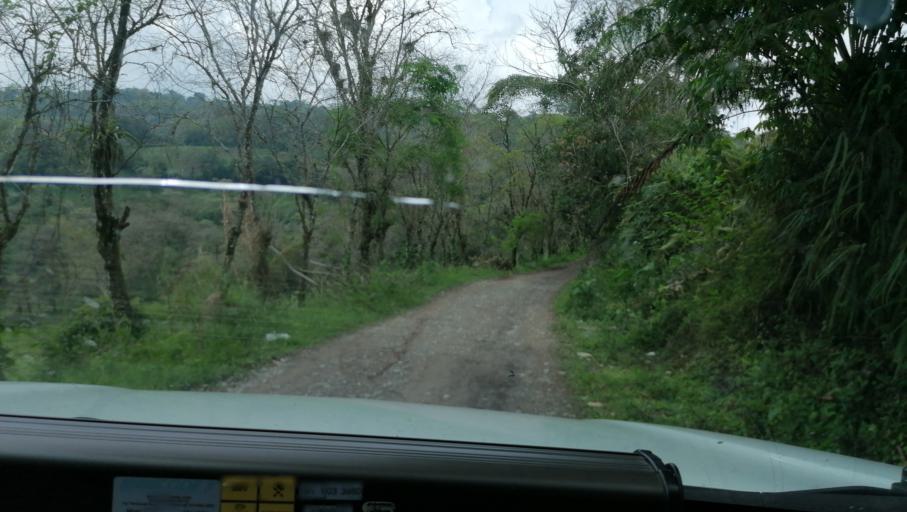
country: MX
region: Chiapas
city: Ocotepec
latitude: 17.3259
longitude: -93.1325
